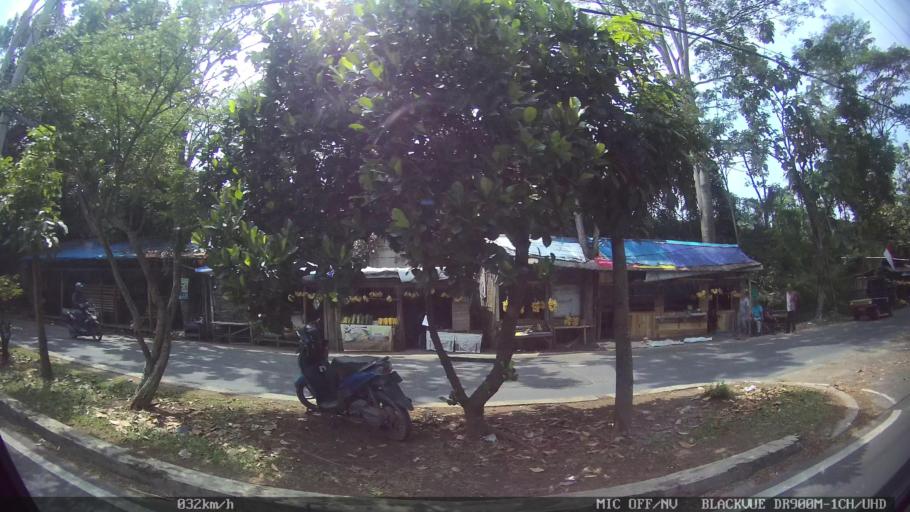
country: ID
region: Lampung
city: Bandarlampung
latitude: -5.4263
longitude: 105.2464
